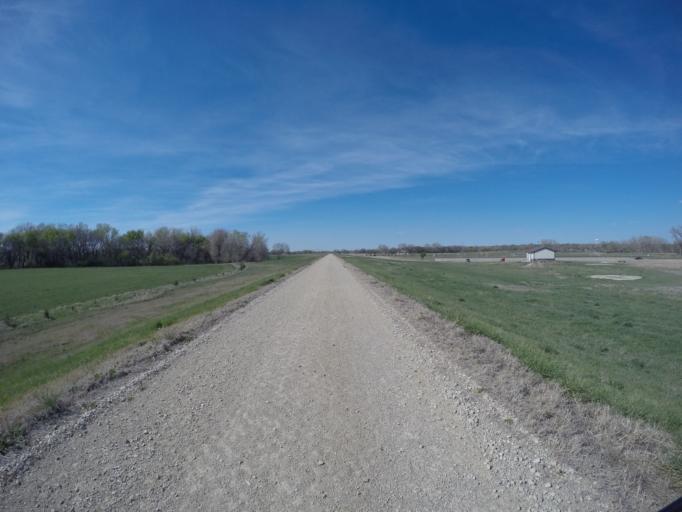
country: US
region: Kansas
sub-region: Saline County
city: Salina
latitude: 38.7935
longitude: -97.5774
